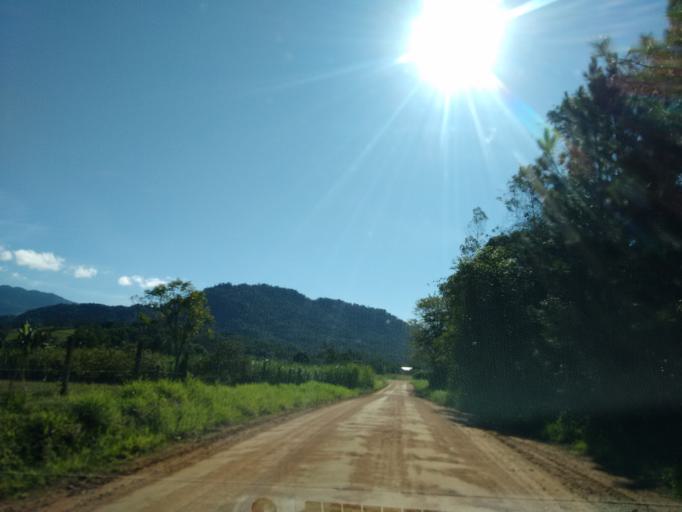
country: BR
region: Santa Catarina
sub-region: Pomerode
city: Pomerode
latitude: -26.6869
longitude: -49.1462
